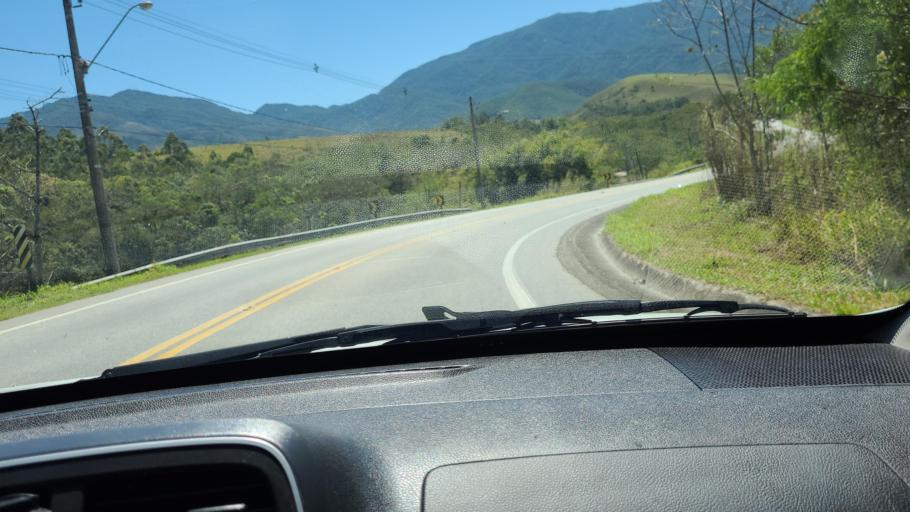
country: BR
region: Sao Paulo
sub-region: Tremembe
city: Tremembe
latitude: -22.8703
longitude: -45.5835
